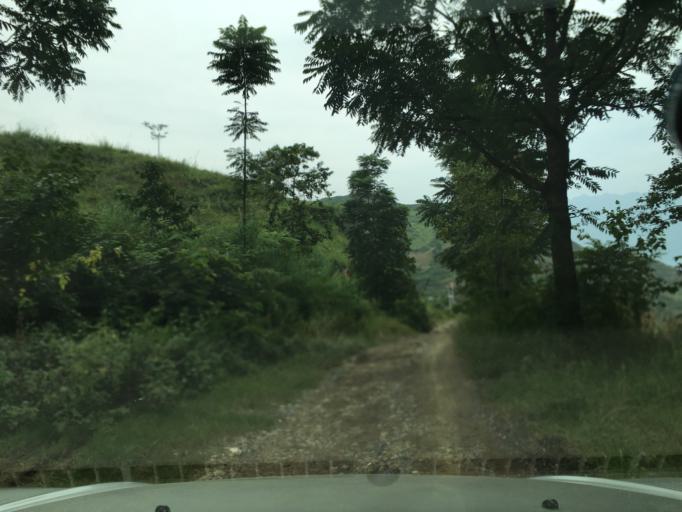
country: CN
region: Guizhou Sheng
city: Liupanshui
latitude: 26.0360
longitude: 105.1863
